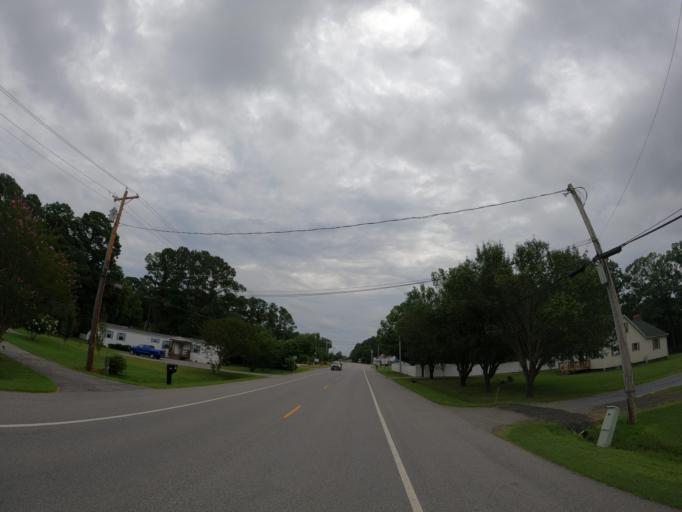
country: US
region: Maryland
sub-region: Saint Mary's County
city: Lexington Park
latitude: 38.1481
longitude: -76.5126
